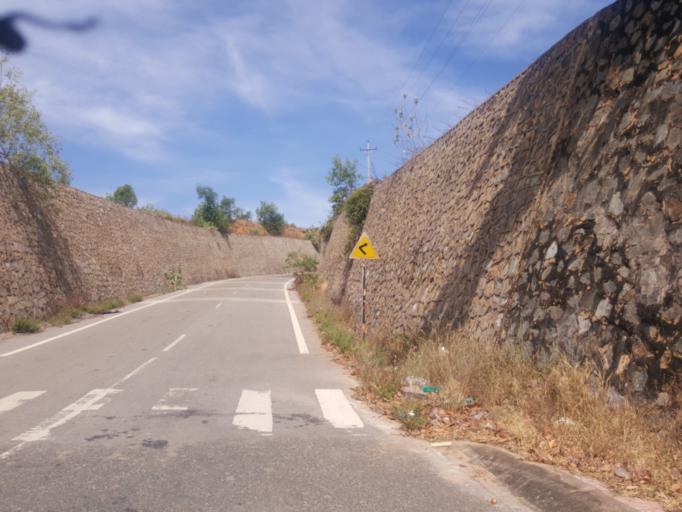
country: VN
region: Binh Thuan
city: Phan Thiet
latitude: 10.9579
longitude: 108.2146
